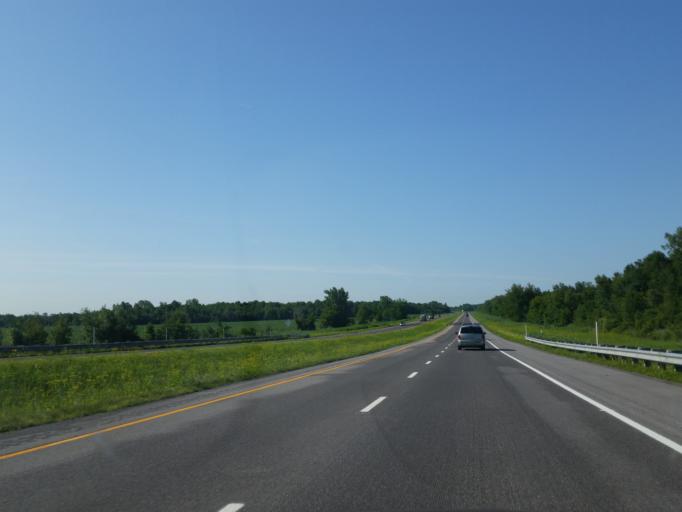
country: CA
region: Quebec
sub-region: Monteregie
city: Napierville
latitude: 45.2362
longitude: -73.4744
